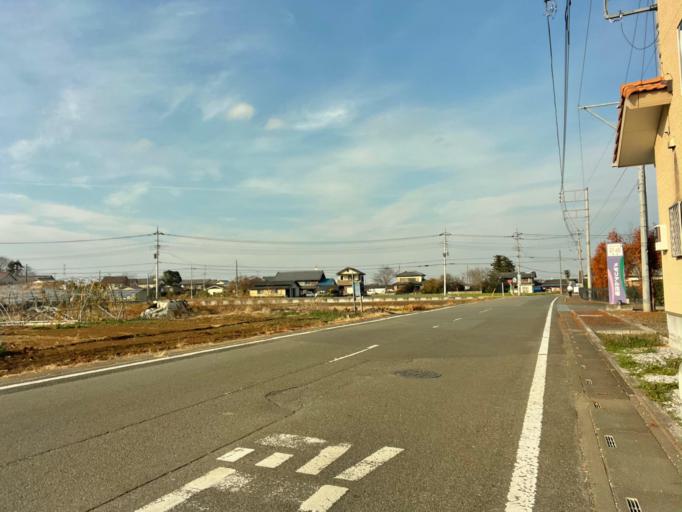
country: JP
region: Saitama
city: Kodamacho-kodamaminami
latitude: 36.1720
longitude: 139.1766
